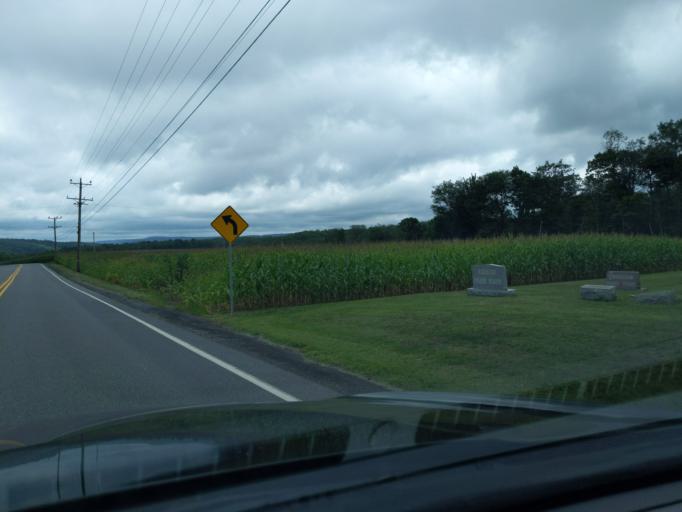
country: US
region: Pennsylvania
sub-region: Cambria County
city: Portage
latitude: 40.3164
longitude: -78.5728
